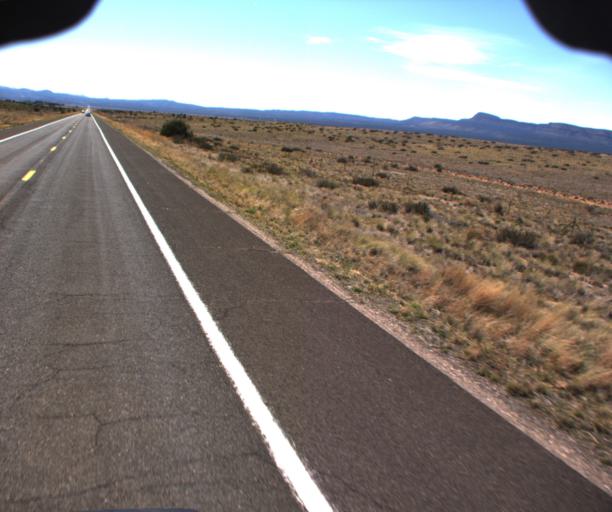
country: US
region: Arizona
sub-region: Mohave County
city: Peach Springs
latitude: 35.5119
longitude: -113.5074
